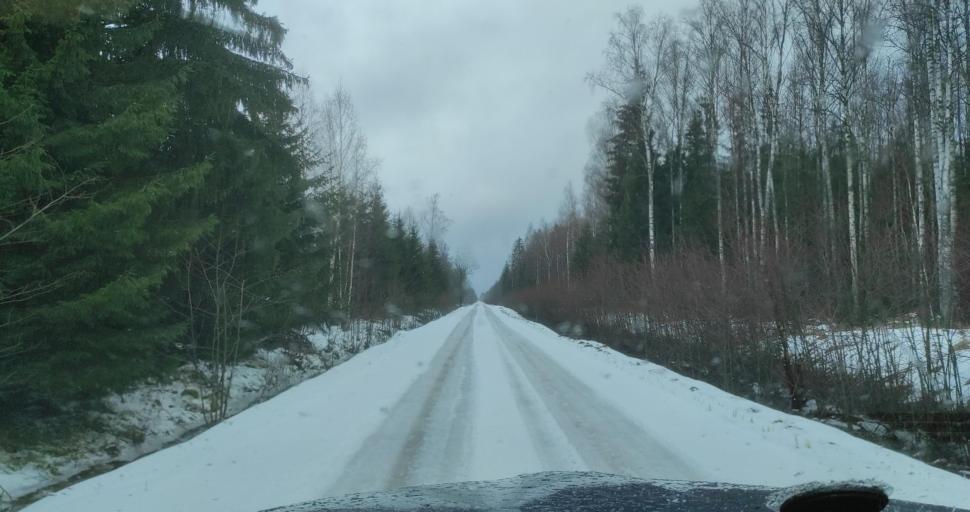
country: LV
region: Dundaga
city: Dundaga
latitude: 57.3914
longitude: 22.1299
